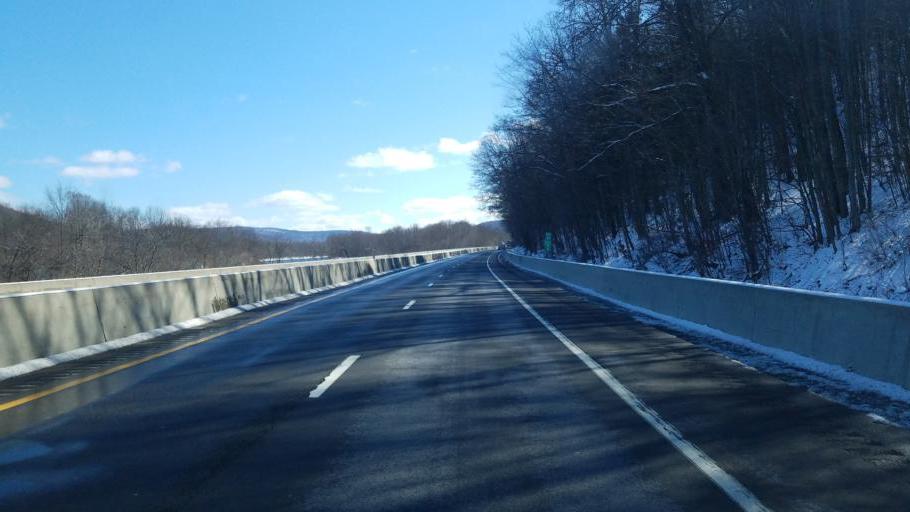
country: US
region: New York
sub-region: Cattaraugus County
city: Salamanca
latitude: 42.1204
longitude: -78.6644
